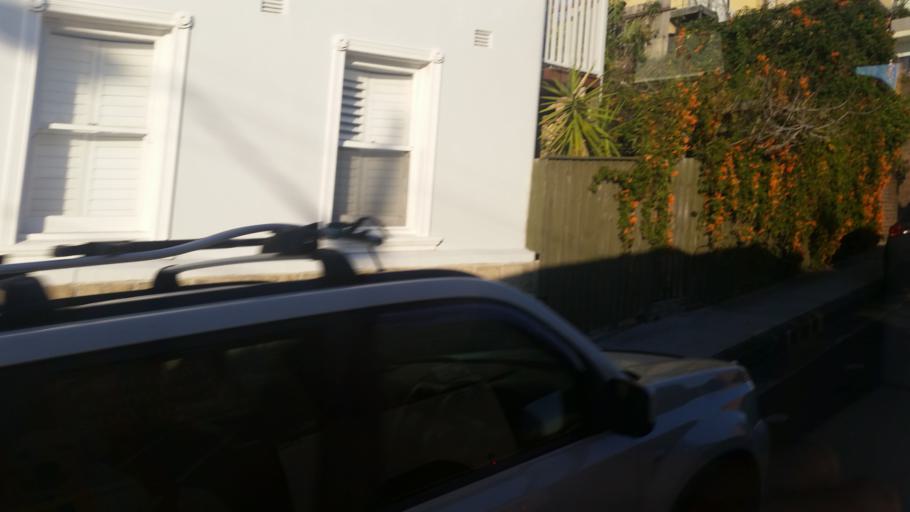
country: AU
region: New South Wales
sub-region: Waverley
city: Bronte
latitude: -33.9064
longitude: 151.2649
